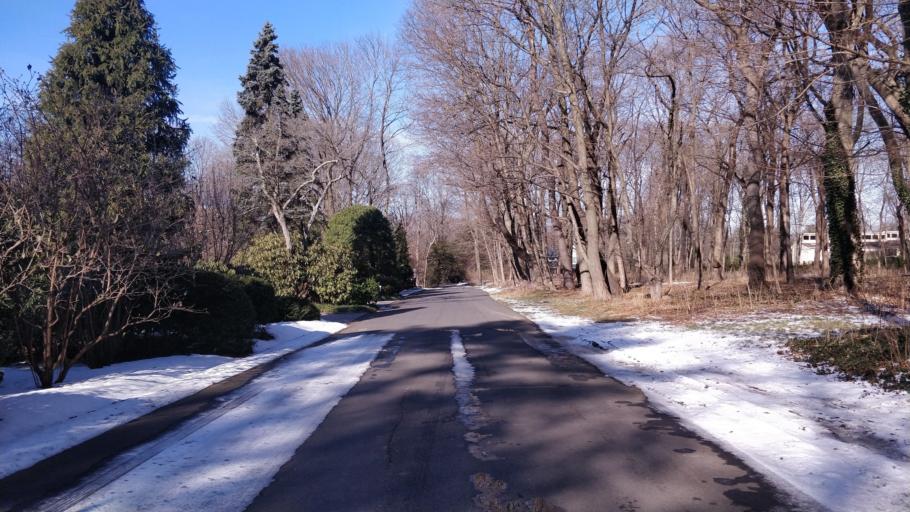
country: US
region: New York
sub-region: Nassau County
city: Old Brookville
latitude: 40.8438
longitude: -73.6111
